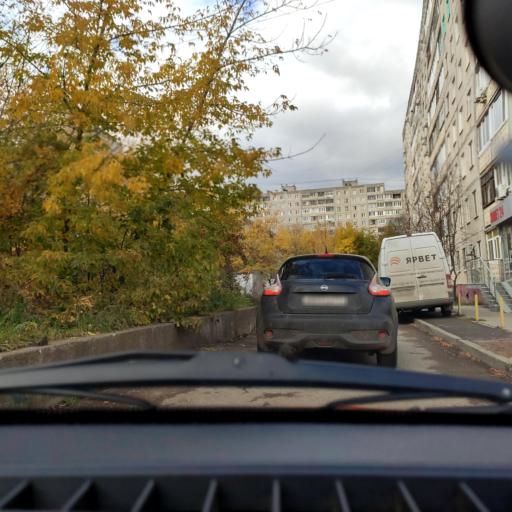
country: RU
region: Bashkortostan
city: Ufa
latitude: 54.7848
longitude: 56.0472
